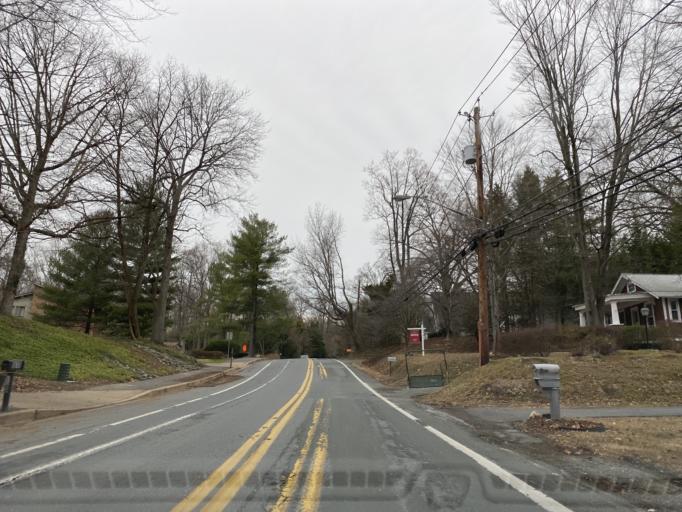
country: US
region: Maryland
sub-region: Montgomery County
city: Cabin John
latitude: 38.9761
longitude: -77.1689
